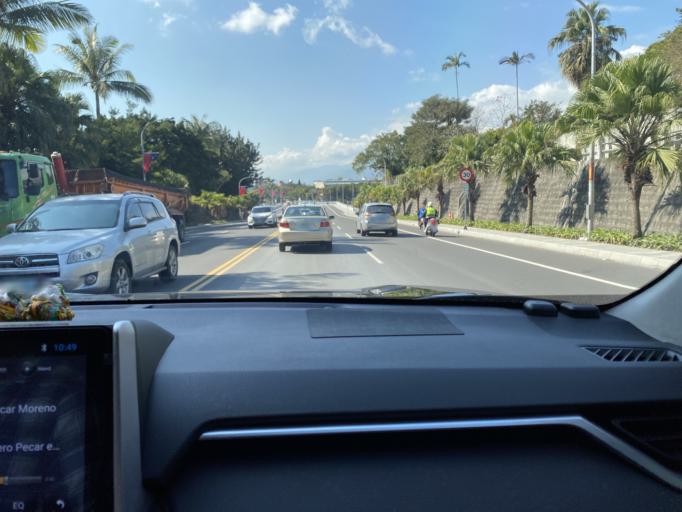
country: TW
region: Taiwan
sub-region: Hualien
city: Hualian
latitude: 23.9809
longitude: 121.6194
